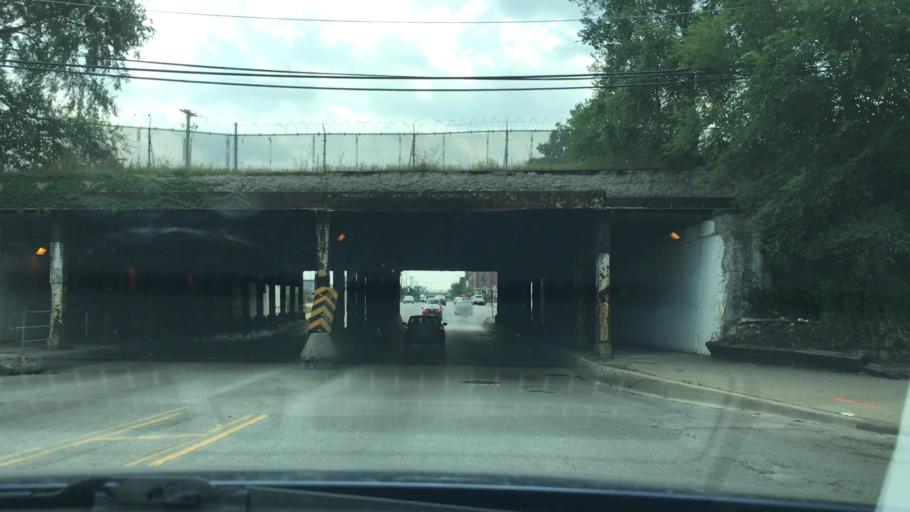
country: US
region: Illinois
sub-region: Cook County
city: Chicago
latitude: 41.8639
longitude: -87.6860
